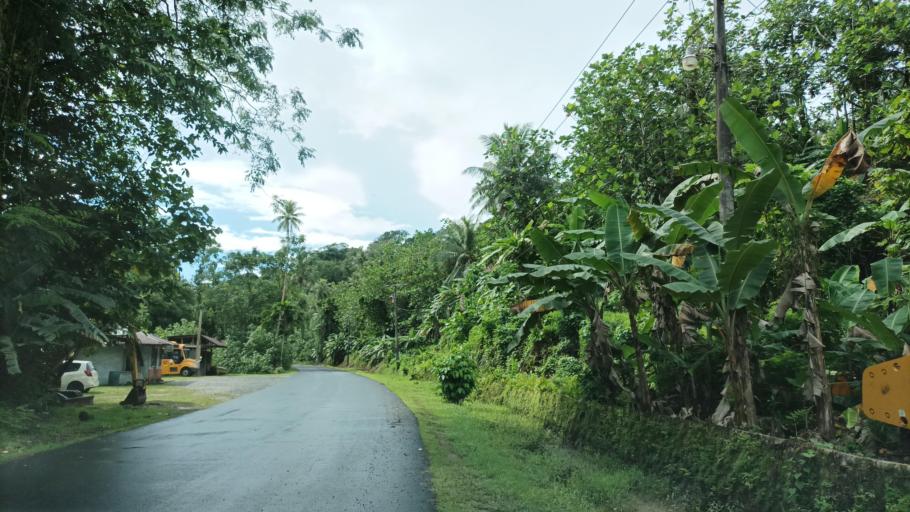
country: FM
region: Pohnpei
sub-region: Madolenihm Municipality
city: Madolenihm Municipality Government
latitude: 6.9147
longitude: 158.3211
